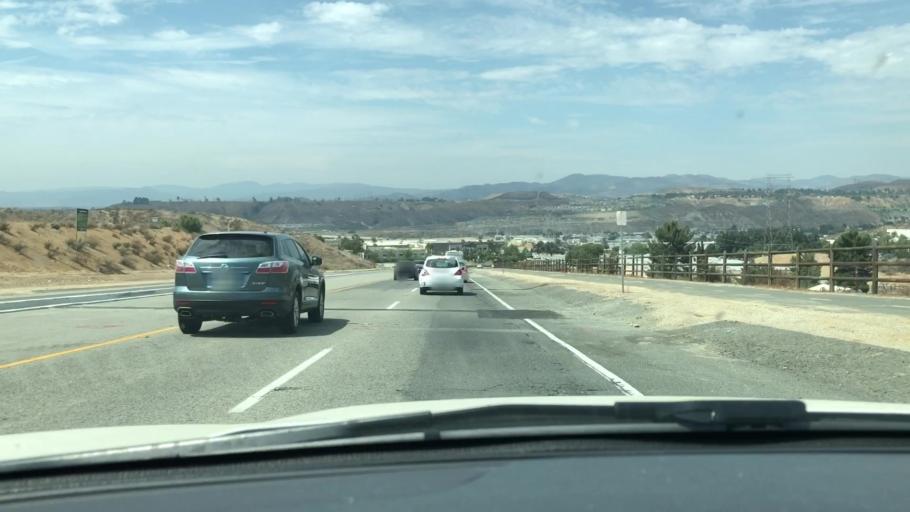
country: US
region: California
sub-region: Los Angeles County
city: Santa Clarita
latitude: 34.4072
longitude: -118.5031
